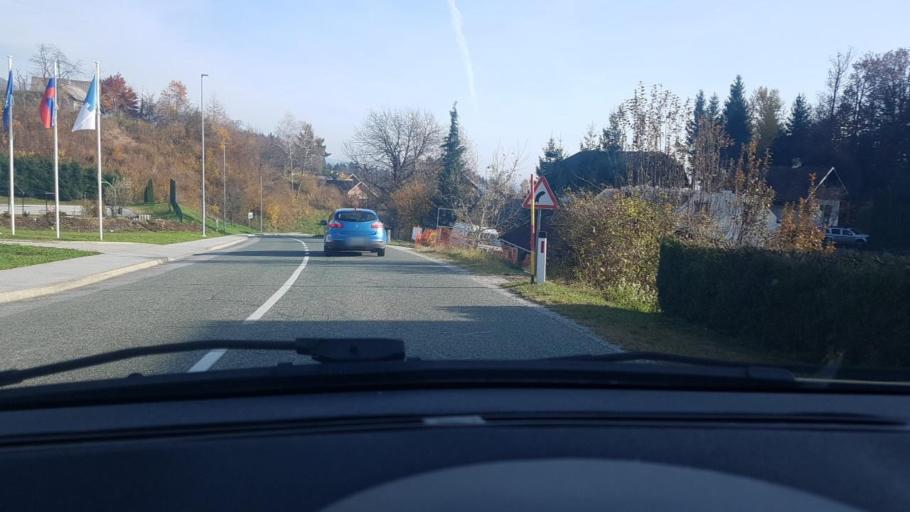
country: SI
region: Kranj
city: Golnik
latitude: 46.3324
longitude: 14.3160
